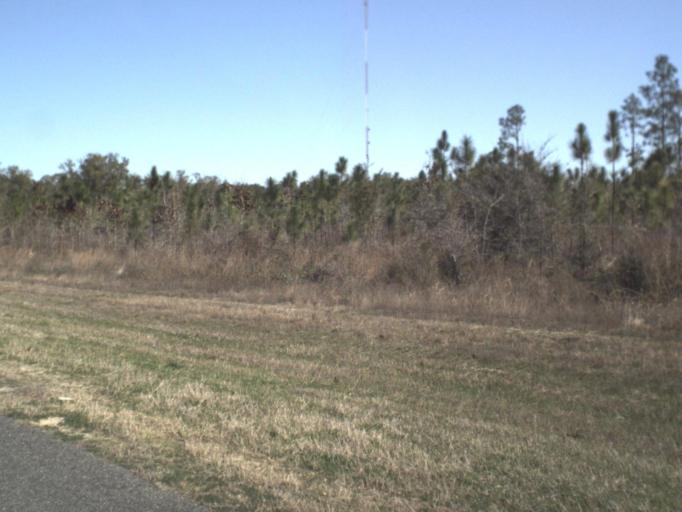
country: US
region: Florida
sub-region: Bay County
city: Youngstown
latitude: 30.4343
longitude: -85.5320
